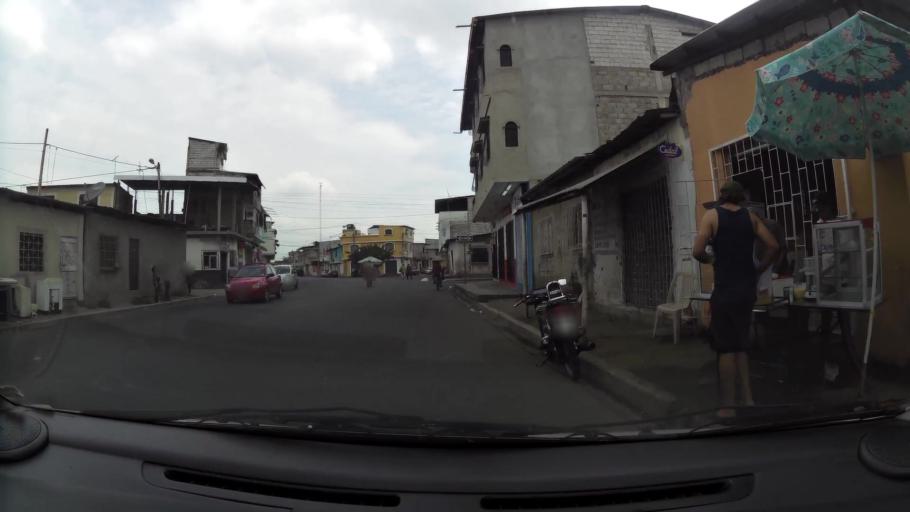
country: EC
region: Guayas
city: Guayaquil
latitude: -2.2295
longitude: -79.9107
